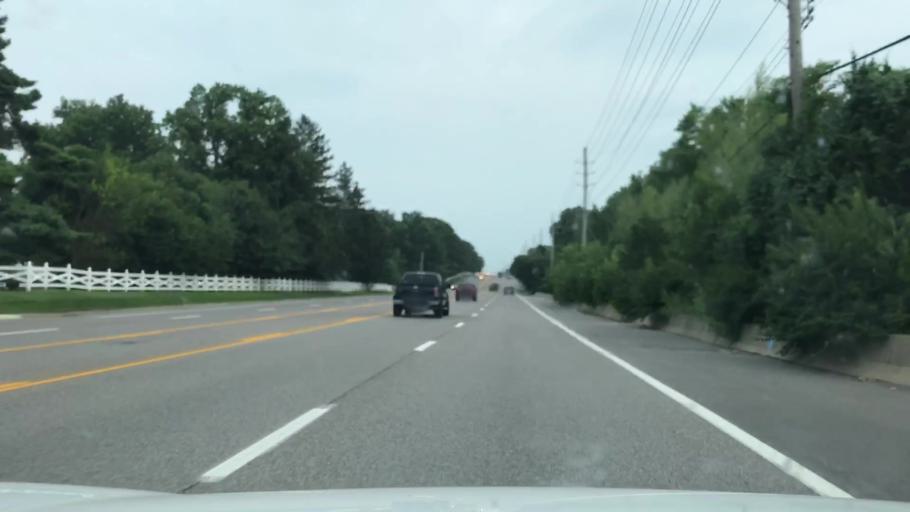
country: US
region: Missouri
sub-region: Saint Louis County
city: Clarkson Valley
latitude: 38.6144
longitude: -90.5857
